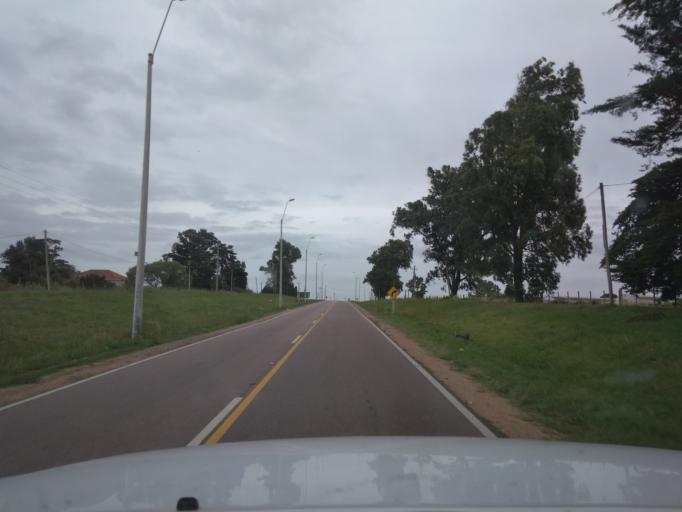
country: UY
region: Canelones
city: Tala
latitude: -34.3586
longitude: -55.7736
